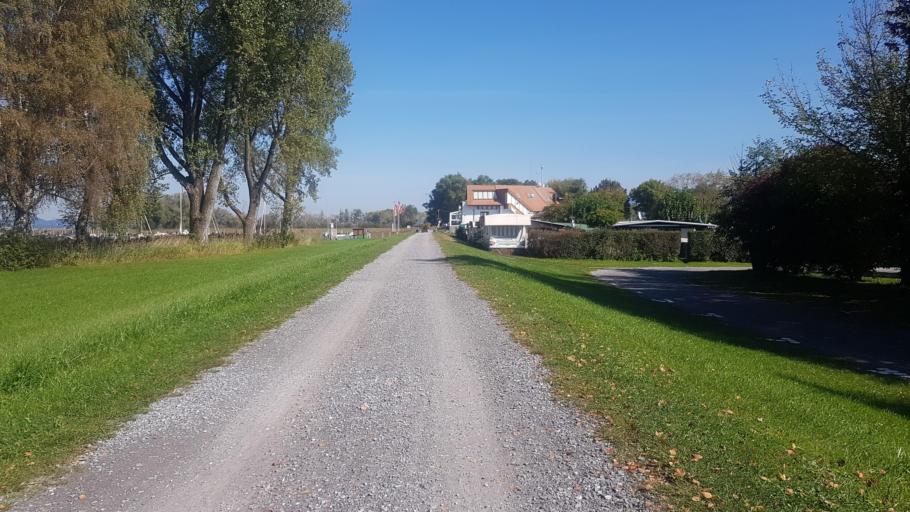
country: AT
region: Vorarlberg
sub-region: Politischer Bezirk Bregenz
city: Fussach
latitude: 47.4966
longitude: 9.6291
